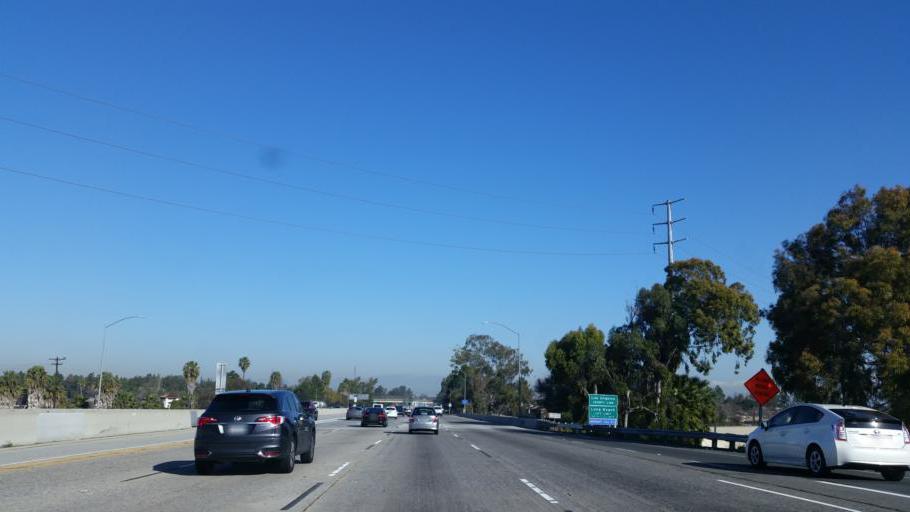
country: US
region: California
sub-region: Orange County
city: Los Alamitos
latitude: 33.8051
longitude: -118.0813
